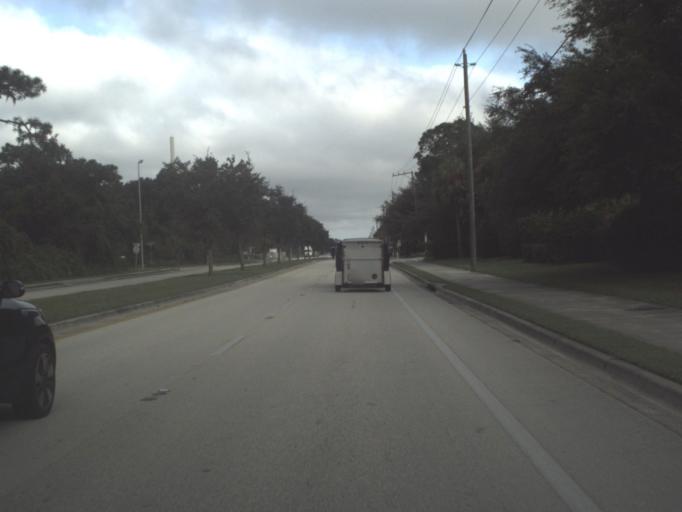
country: US
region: Florida
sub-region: Sarasota County
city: Englewood
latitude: 26.9828
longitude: -82.3612
